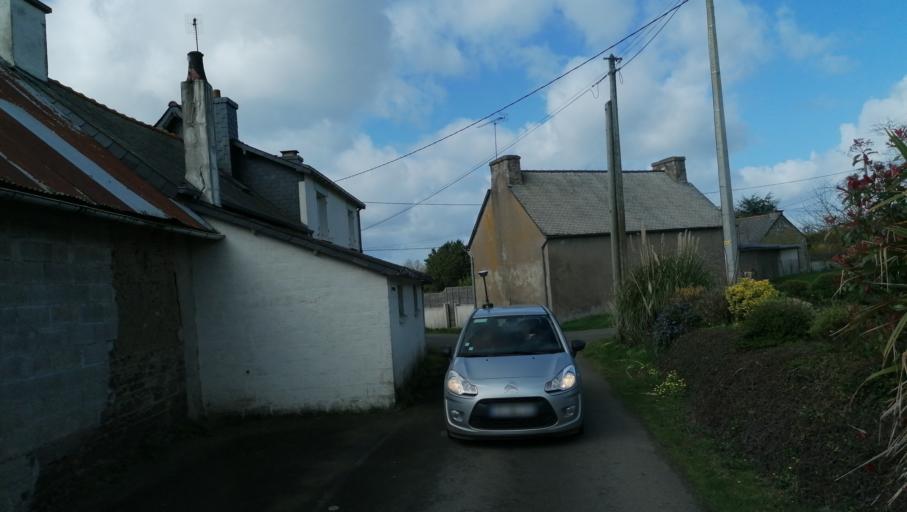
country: FR
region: Brittany
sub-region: Departement des Cotes-d'Armor
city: Pleguien
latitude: 48.6327
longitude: -2.9219
